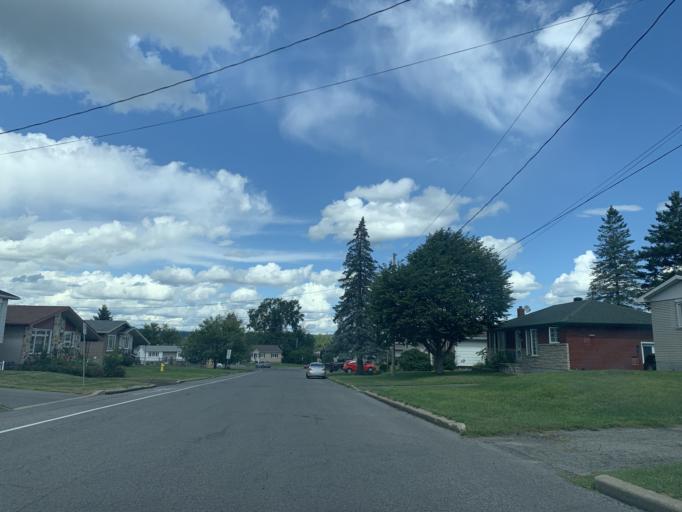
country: CA
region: Ontario
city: Hawkesbury
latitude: 45.6068
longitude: -74.5996
